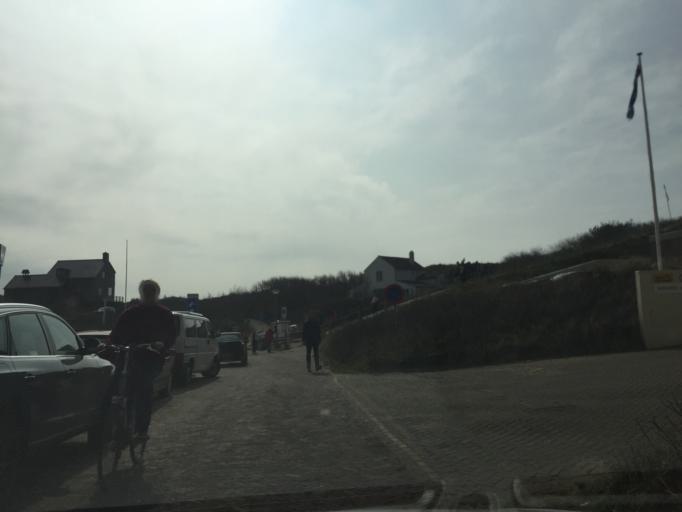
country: NL
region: North Holland
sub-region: Gemeente Bergen
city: Egmond aan Zee
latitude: 52.6578
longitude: 4.6293
